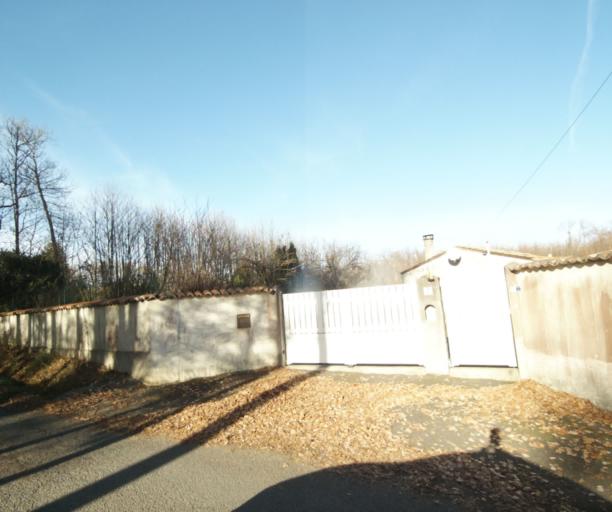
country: FR
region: Poitou-Charentes
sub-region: Departement de la Charente-Maritime
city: Burie
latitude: 45.7740
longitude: -0.4294
